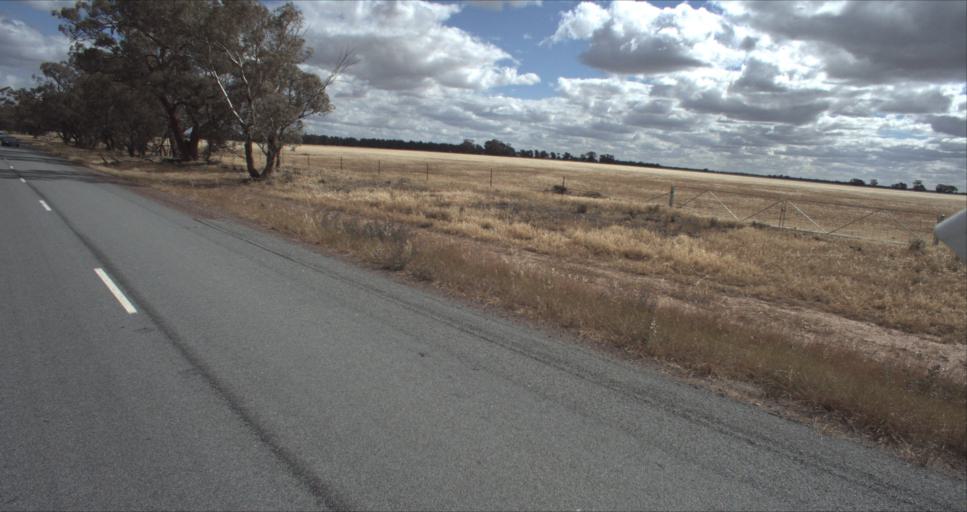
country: AU
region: New South Wales
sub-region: Leeton
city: Leeton
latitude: -34.6766
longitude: 146.3464
